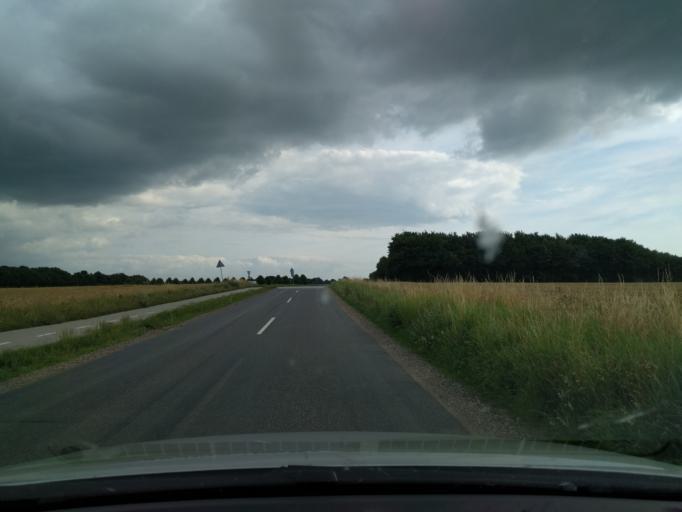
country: DK
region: Central Jutland
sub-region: Herning Kommune
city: Snejbjerg
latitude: 56.1033
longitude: 8.9092
